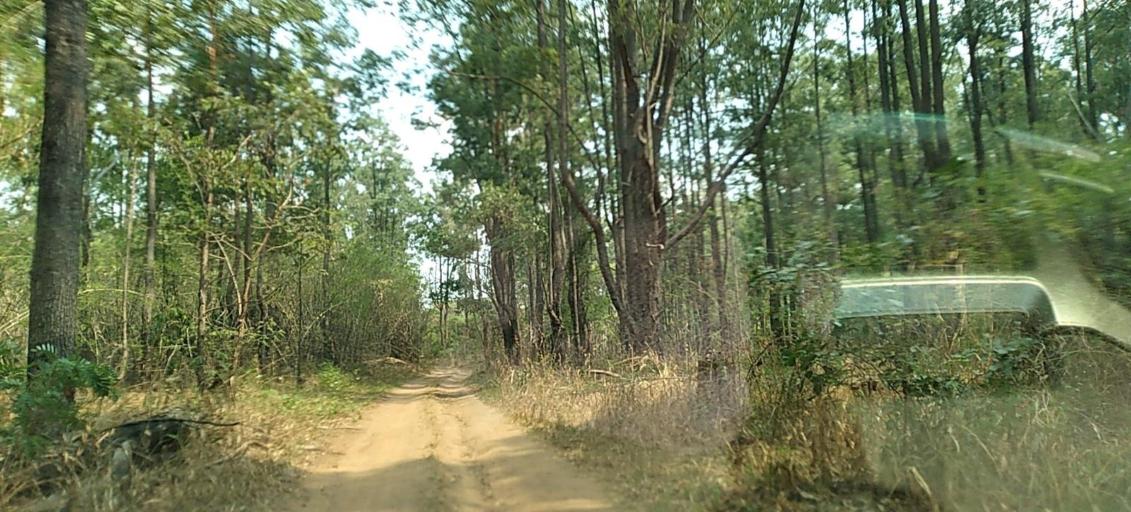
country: ZM
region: Copperbelt
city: Chingola
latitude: -12.7389
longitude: 27.7594
